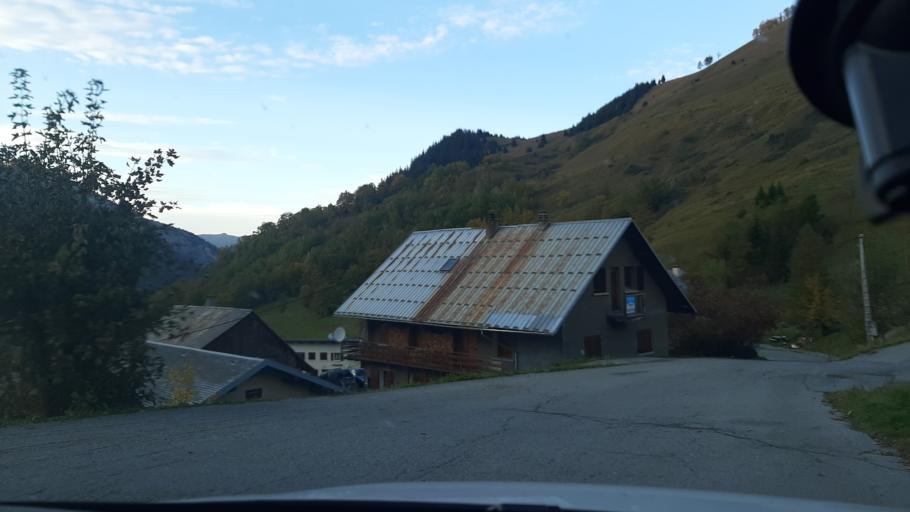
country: FR
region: Rhone-Alpes
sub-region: Departement de la Savoie
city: Villargondran
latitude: 45.1848
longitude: 6.3175
